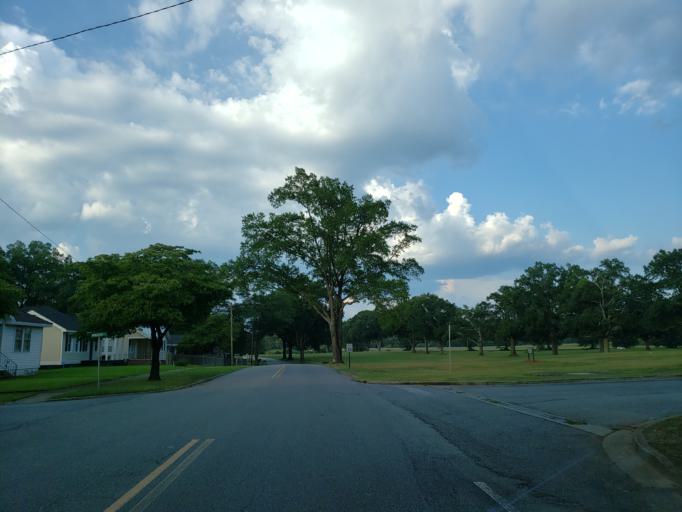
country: US
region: Georgia
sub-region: Polk County
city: Rockmart
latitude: 34.0035
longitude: -85.0330
